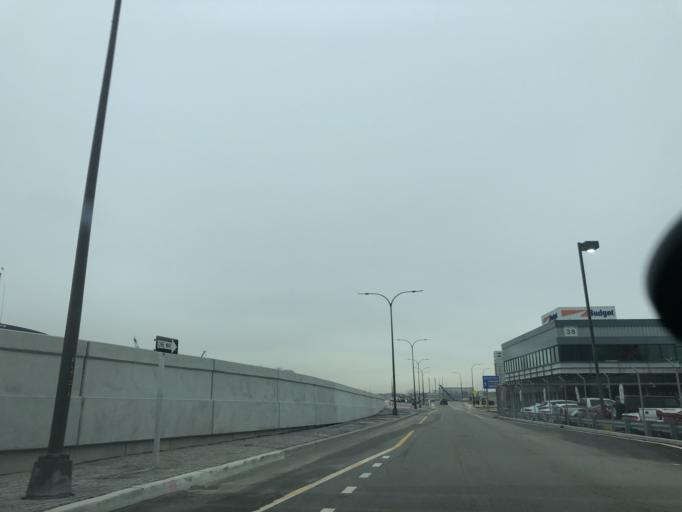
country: US
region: New Jersey
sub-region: Union County
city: Elizabeth
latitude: 40.6884
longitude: -74.1900
